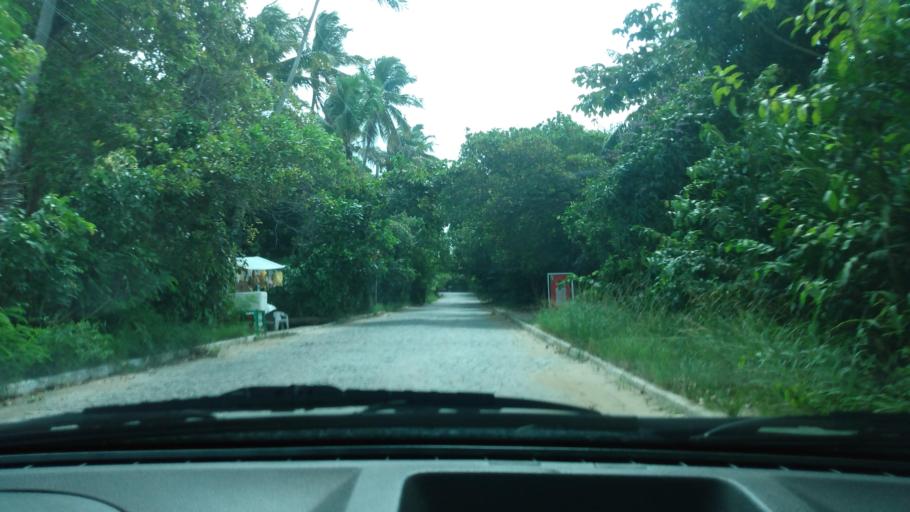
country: BR
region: Pernambuco
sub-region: Cabo De Santo Agostinho
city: Cabo
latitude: -8.3473
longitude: -34.9540
